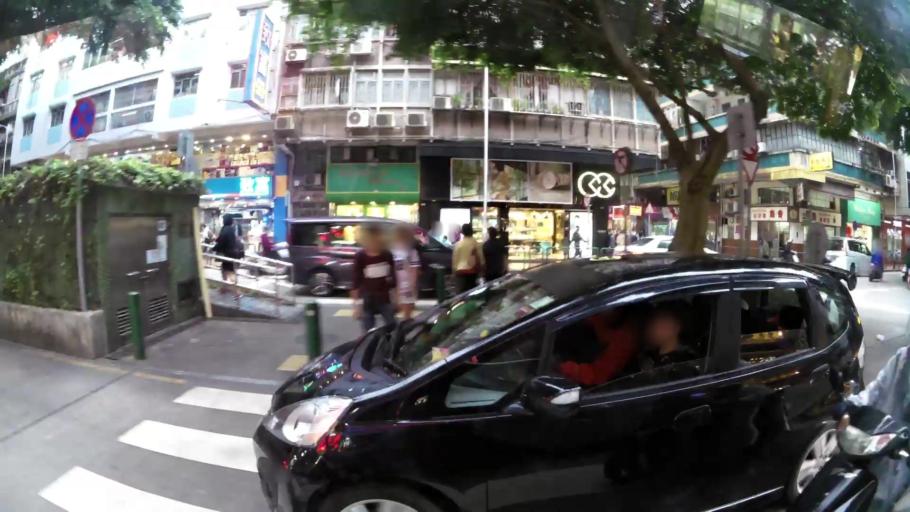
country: MO
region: Macau
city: Macau
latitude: 22.2037
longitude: 113.5462
